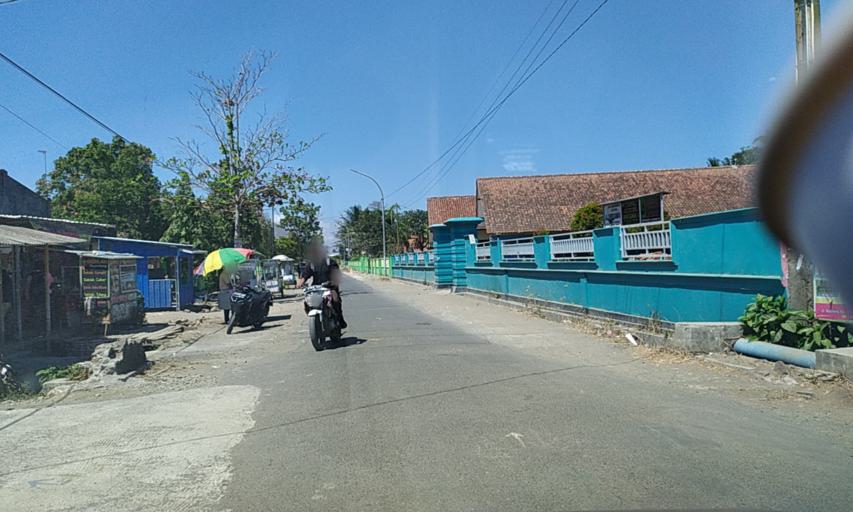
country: ID
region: Central Java
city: Adipala
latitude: -7.6613
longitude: 109.1127
